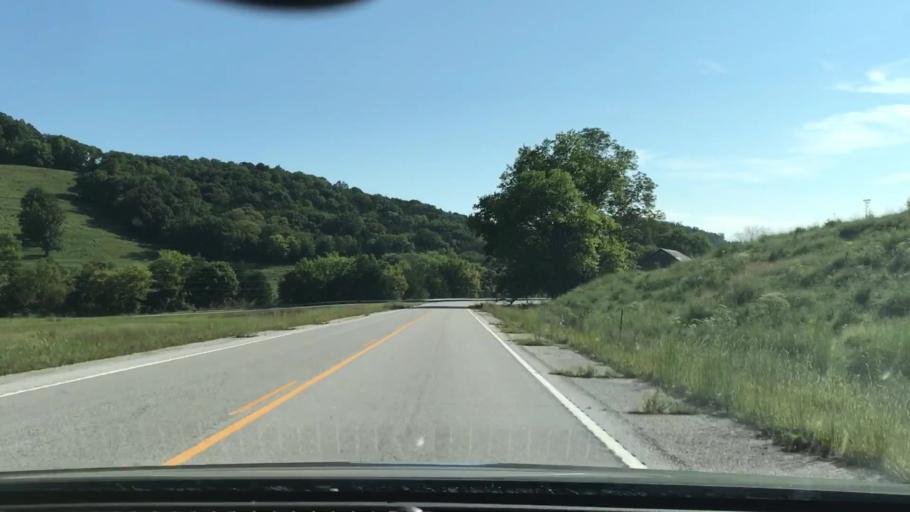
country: US
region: Tennessee
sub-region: Smith County
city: Carthage
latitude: 36.3492
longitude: -85.8274
